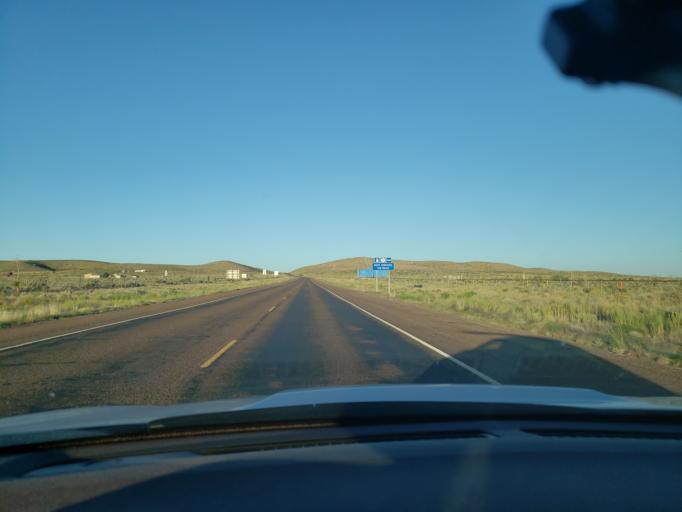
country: US
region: Texas
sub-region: El Paso County
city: Homestead Meadows South
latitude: 31.8267
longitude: -105.9082
